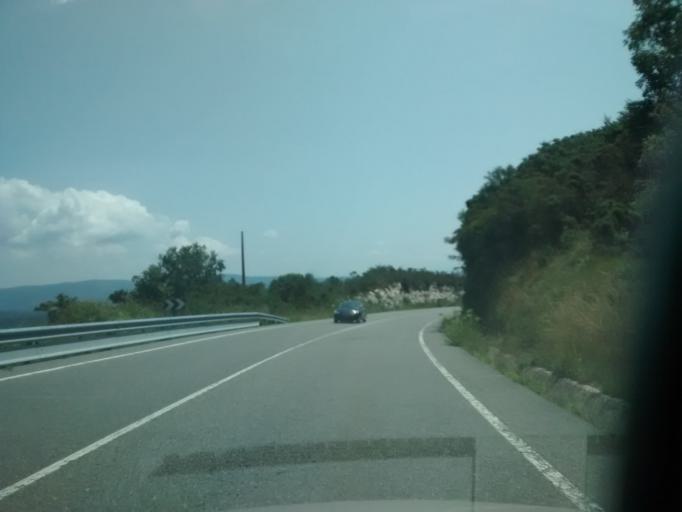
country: ES
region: Galicia
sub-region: Provincia de Ourense
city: Boboras
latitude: 42.4872
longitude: -8.2084
